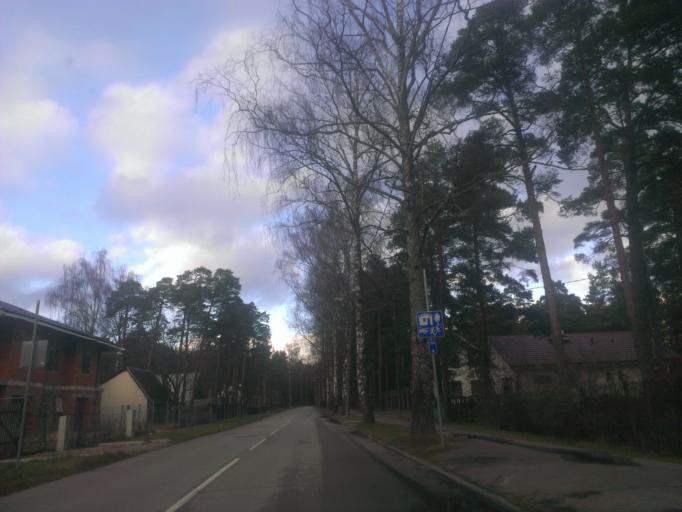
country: LV
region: Riga
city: Bolderaja
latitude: 57.0710
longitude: 24.1049
